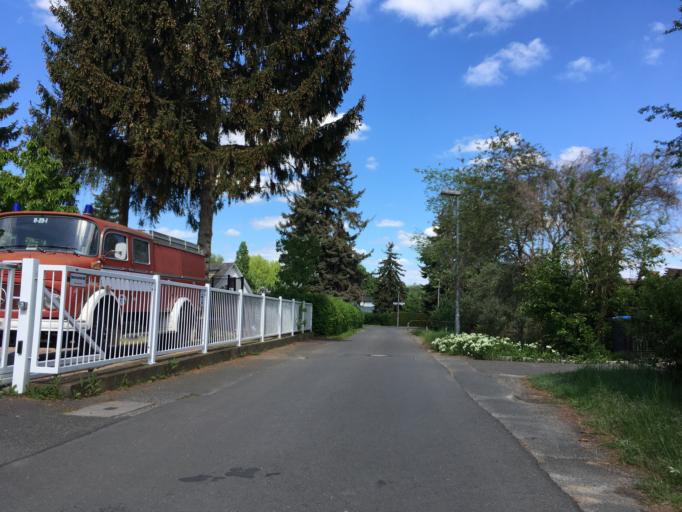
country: DE
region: Berlin
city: Blankenfelde
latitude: 52.6304
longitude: 13.3851
